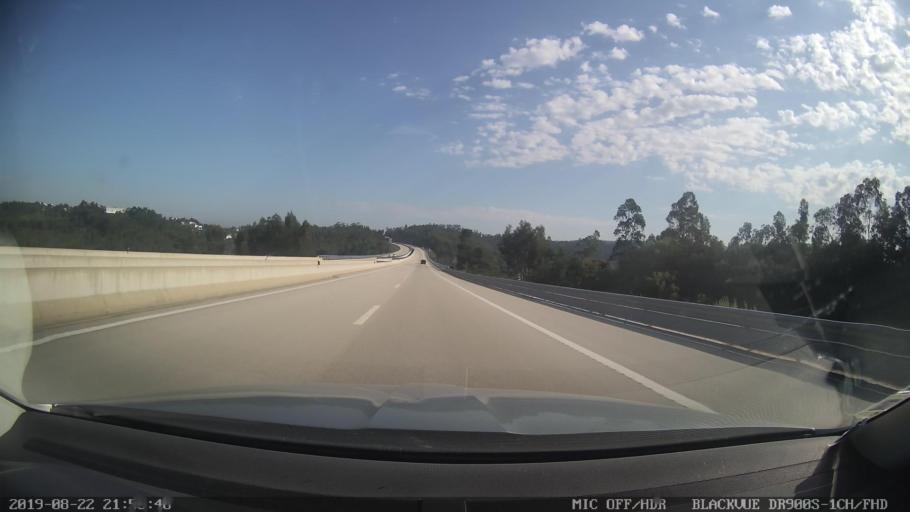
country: PT
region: Coimbra
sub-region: Miranda do Corvo
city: Miranda do Corvo
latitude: 40.1246
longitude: -8.3823
